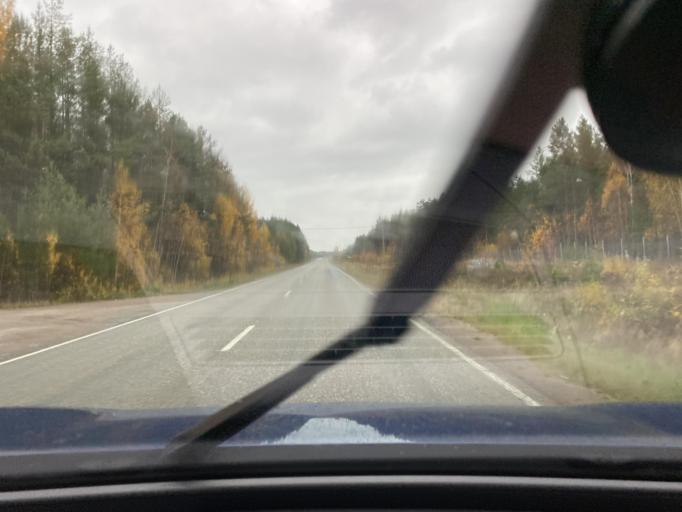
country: FI
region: Satakunta
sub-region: Rauma
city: Saekylae
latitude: 61.0504
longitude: 22.4378
